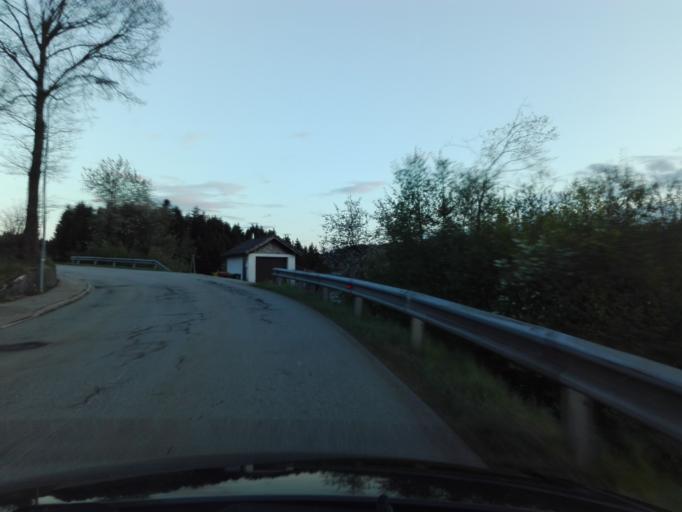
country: DE
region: Bavaria
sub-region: Lower Bavaria
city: Wegscheid
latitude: 48.5504
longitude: 13.7728
